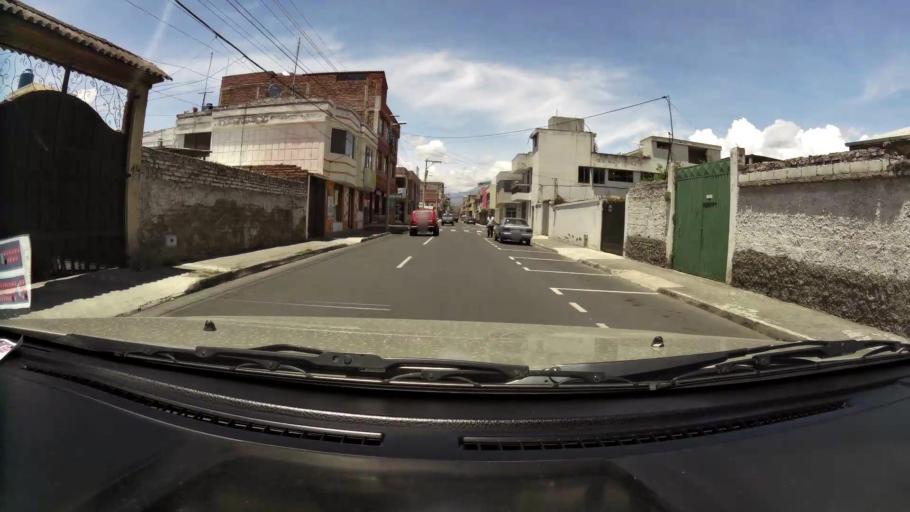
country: EC
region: Chimborazo
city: Riobamba
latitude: -1.6726
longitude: -78.6423
